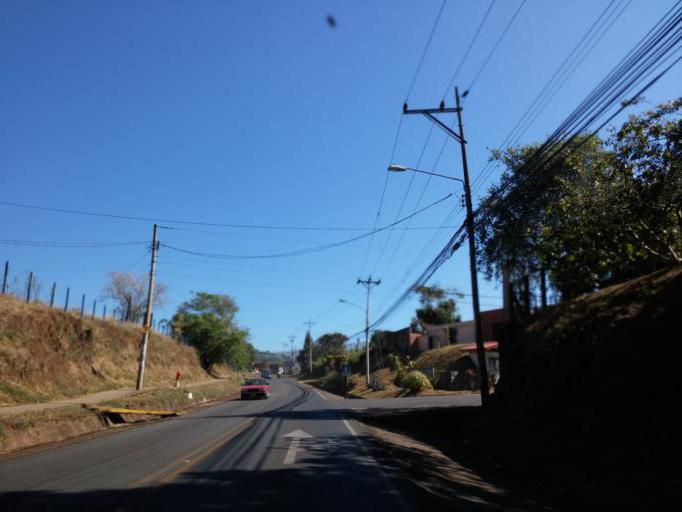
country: CR
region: Alajuela
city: Alajuela
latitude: 10.0332
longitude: -84.2132
